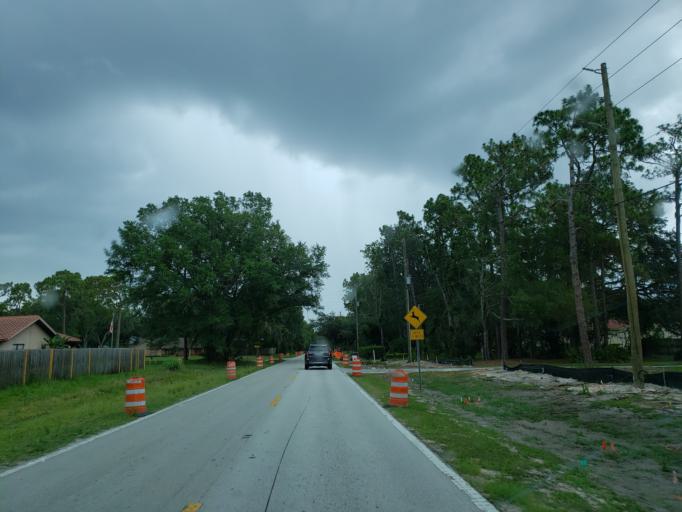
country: US
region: Florida
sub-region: Pasco County
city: Wesley Chapel
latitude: 28.2505
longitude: -82.3543
